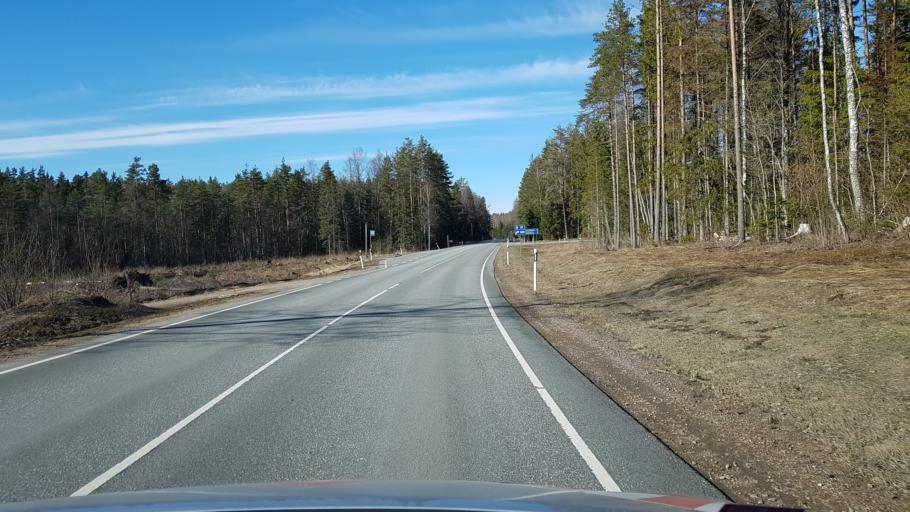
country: EE
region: Laeaene-Virumaa
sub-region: Kadrina vald
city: Kadrina
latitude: 59.3934
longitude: 26.0138
